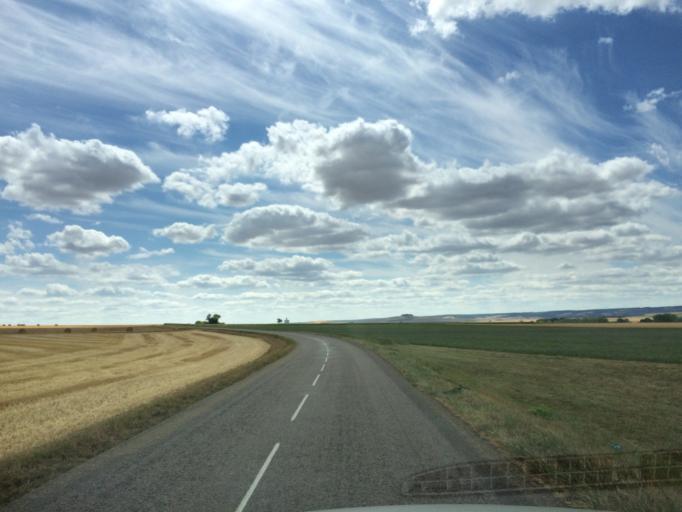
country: FR
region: Bourgogne
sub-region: Departement de l'Yonne
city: Laroche-Saint-Cydroine
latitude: 47.9357
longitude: 3.4617
